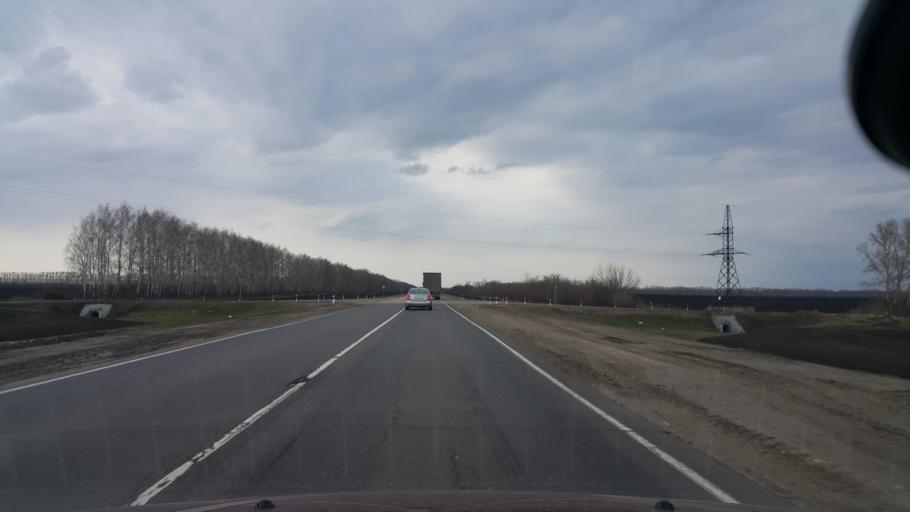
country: RU
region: Tambov
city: Znamenka
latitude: 52.4331
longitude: 41.3733
